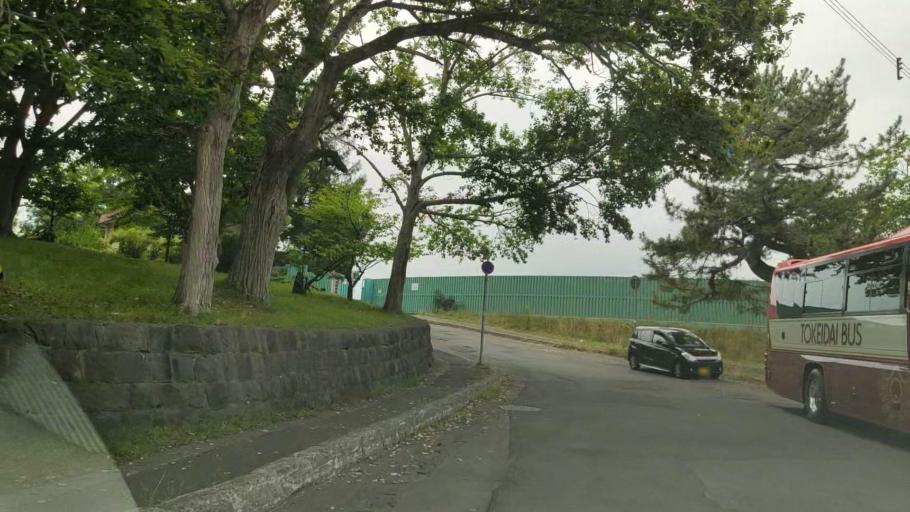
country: JP
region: Hokkaido
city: Otaru
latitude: 43.1874
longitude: 140.9928
